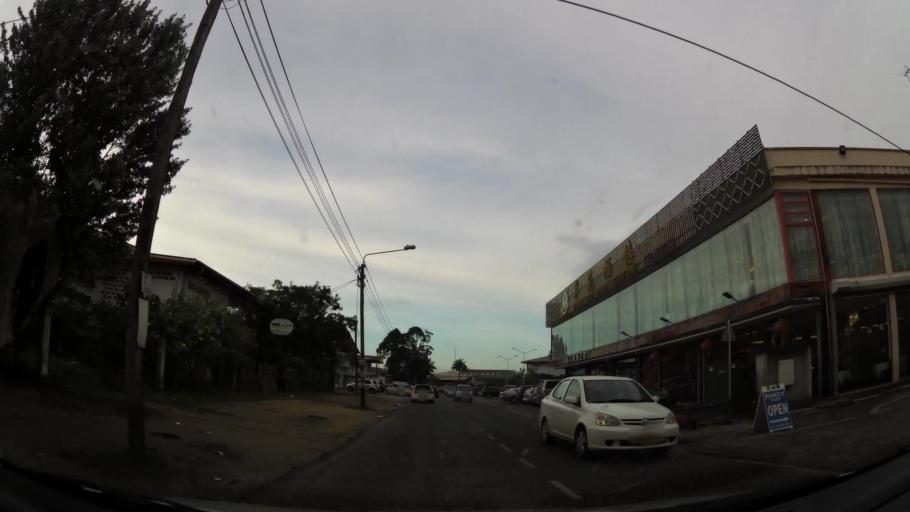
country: SR
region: Paramaribo
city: Paramaribo
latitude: 5.8277
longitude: -55.1910
